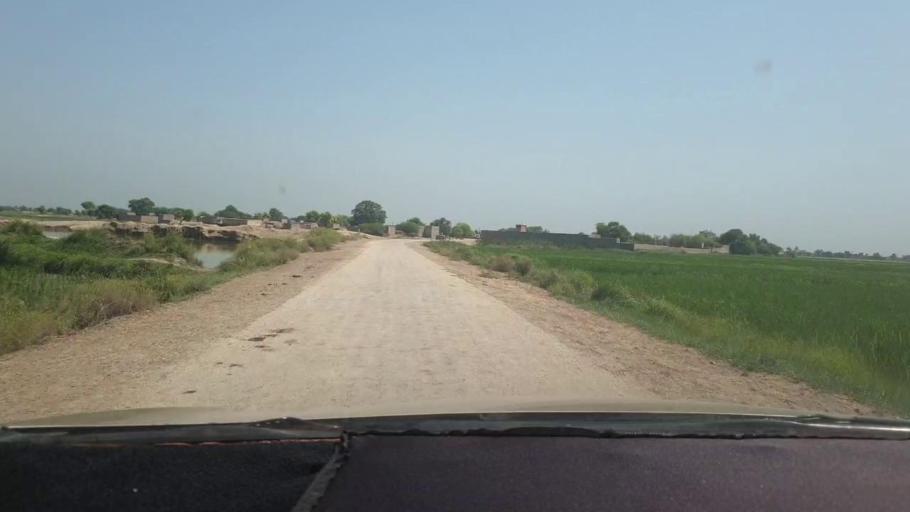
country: PK
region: Sindh
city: Miro Khan
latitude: 27.6727
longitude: 68.0959
